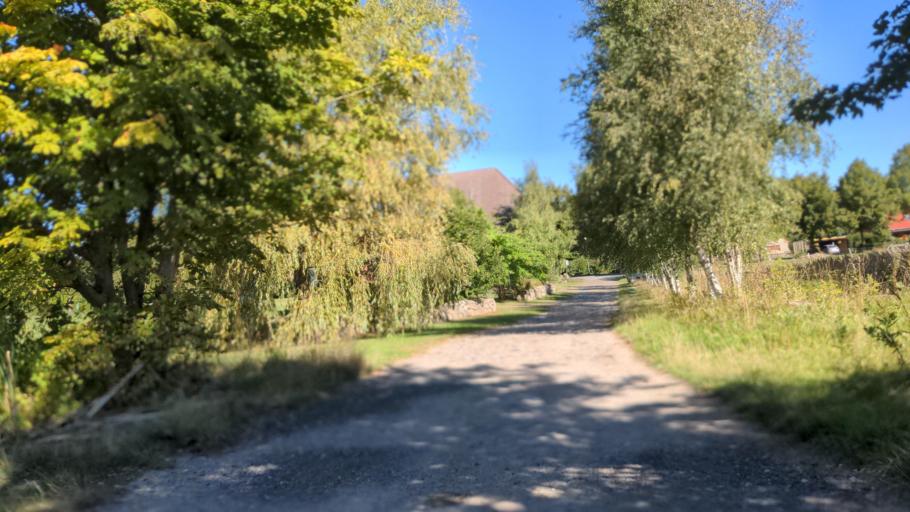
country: DE
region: Mecklenburg-Vorpommern
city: Klutz
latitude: 53.9819
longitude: 11.1379
